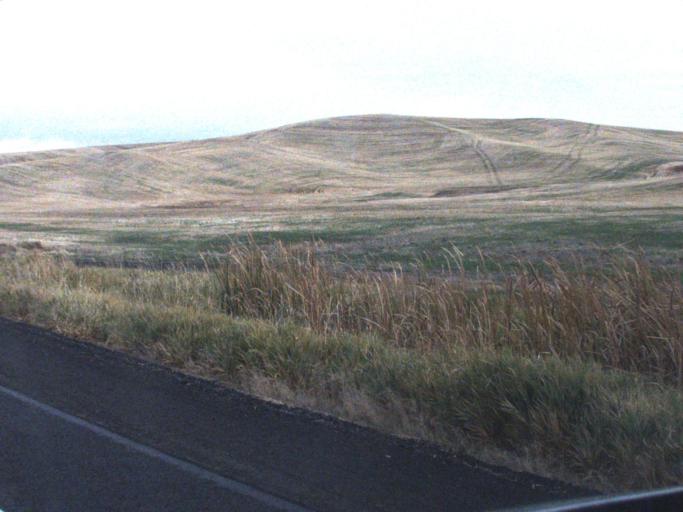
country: US
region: Washington
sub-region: Whitman County
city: Colfax
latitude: 46.8784
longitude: -117.3960
